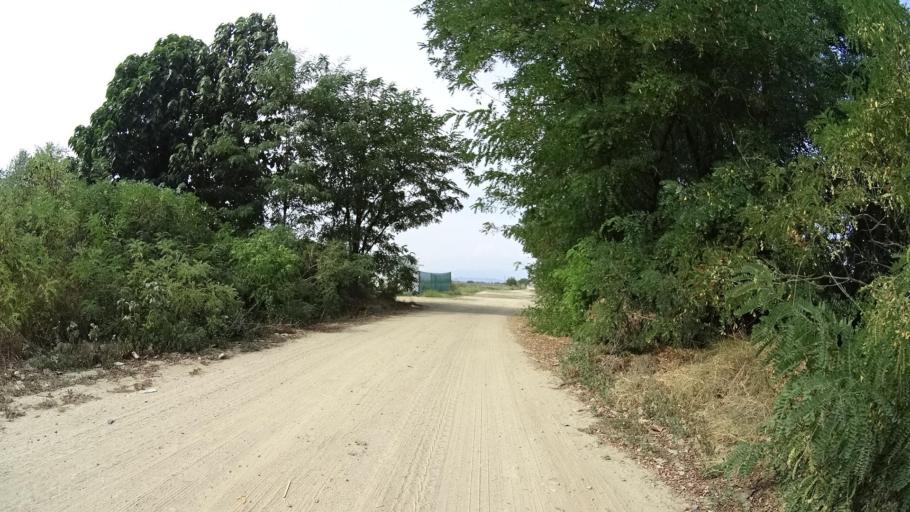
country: BG
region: Plovdiv
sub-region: Obshtina Kaloyanovo
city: Kaloyanovo
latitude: 42.3053
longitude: 24.7994
